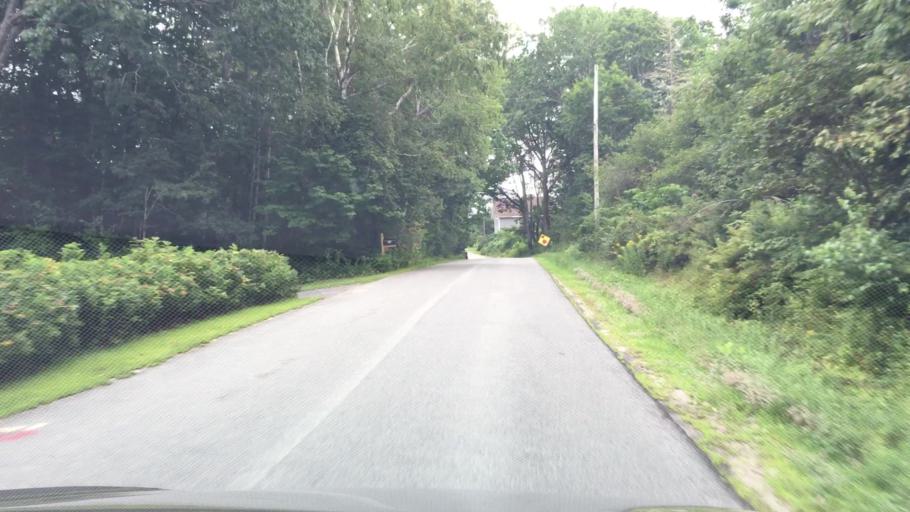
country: US
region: Maine
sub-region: Waldo County
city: Stockton Springs
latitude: 44.5092
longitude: -68.8104
